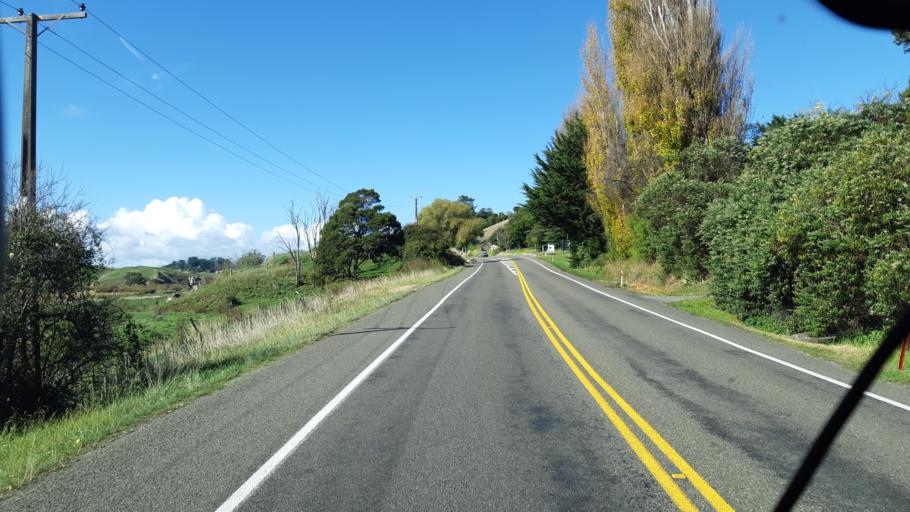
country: NZ
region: Manawatu-Wanganui
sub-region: Wanganui District
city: Wanganui
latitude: -39.9541
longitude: 175.0646
